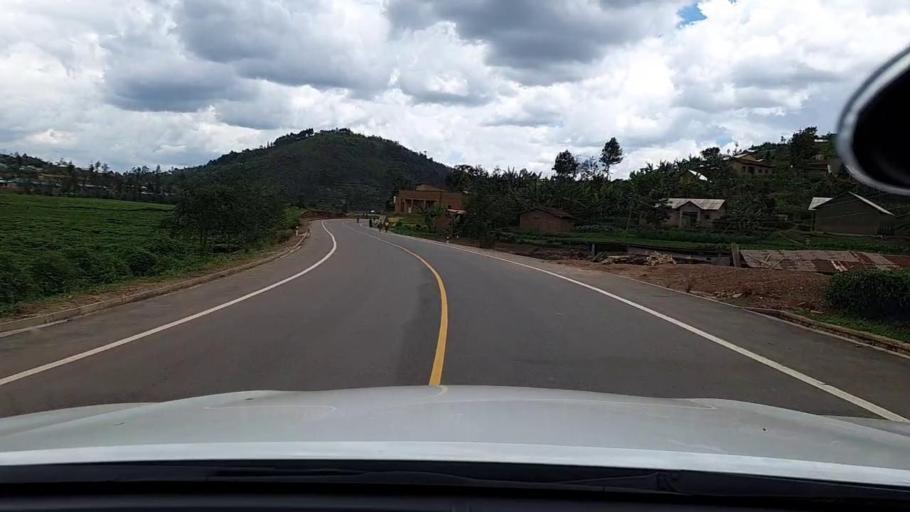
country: RW
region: Northern Province
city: Byumba
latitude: -1.6536
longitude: 29.9041
